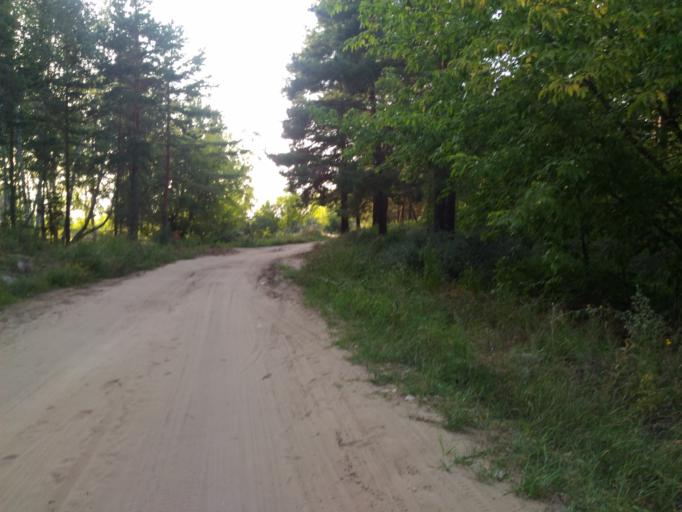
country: RU
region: Ulyanovsk
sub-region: Ulyanovskiy Rayon
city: Ulyanovsk
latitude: 54.3572
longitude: 48.5158
